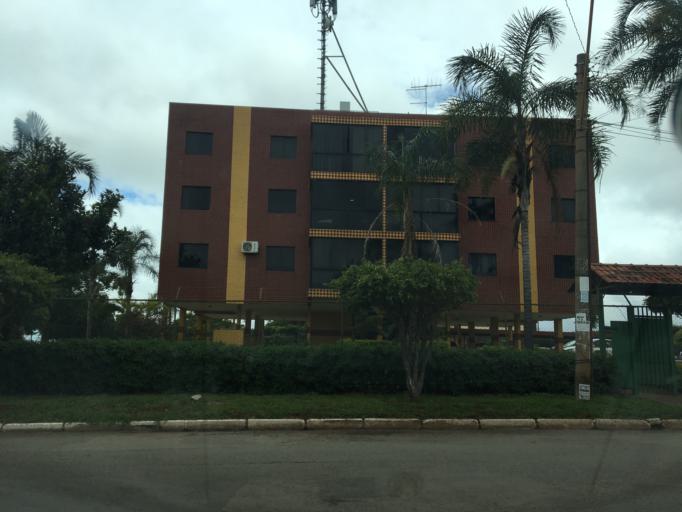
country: BR
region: Federal District
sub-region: Brasilia
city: Brasilia
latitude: -15.8243
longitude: -48.0857
